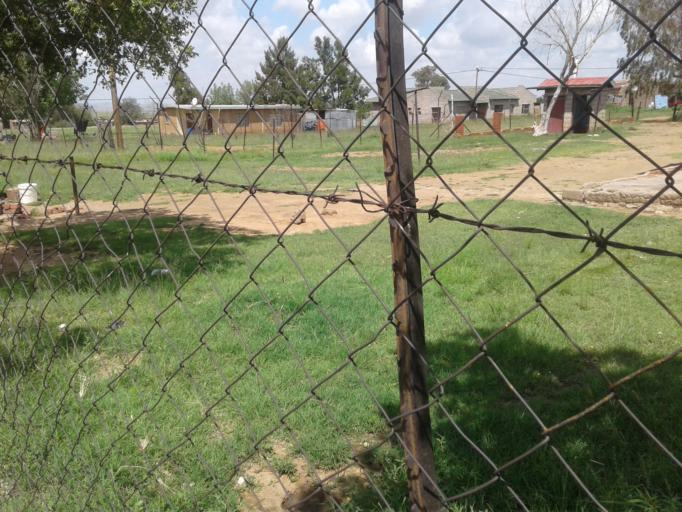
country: LS
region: Mafeteng
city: Mafeteng
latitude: -29.7546
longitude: 27.1124
